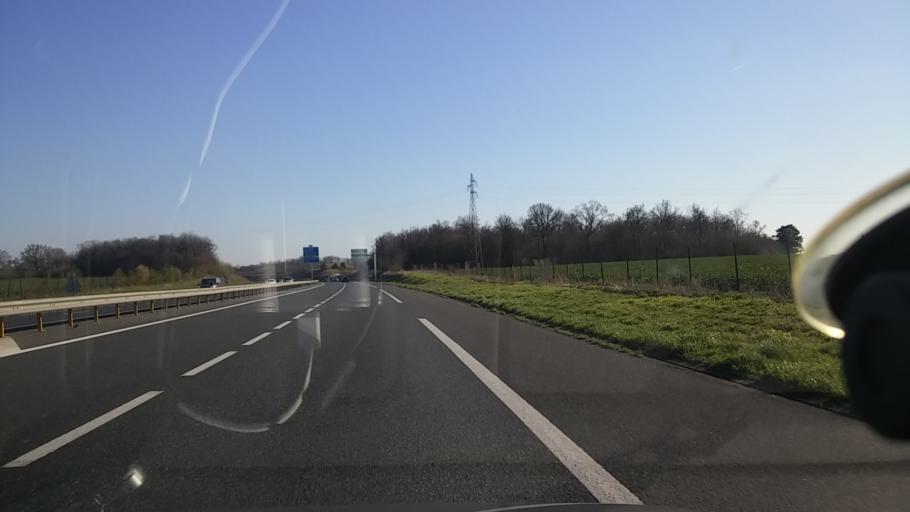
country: FR
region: Centre
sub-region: Departement de l'Indre
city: Saint-Maur
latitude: 46.8010
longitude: 1.6163
